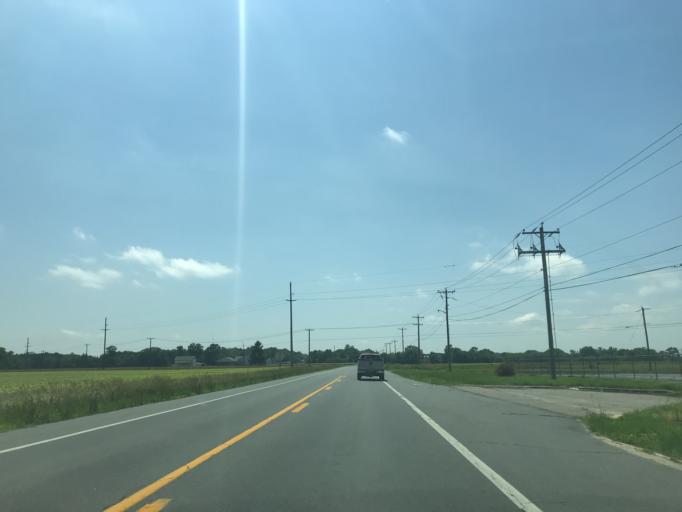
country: US
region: Maryland
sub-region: Dorchester County
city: Hurlock
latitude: 38.5975
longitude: -75.9067
